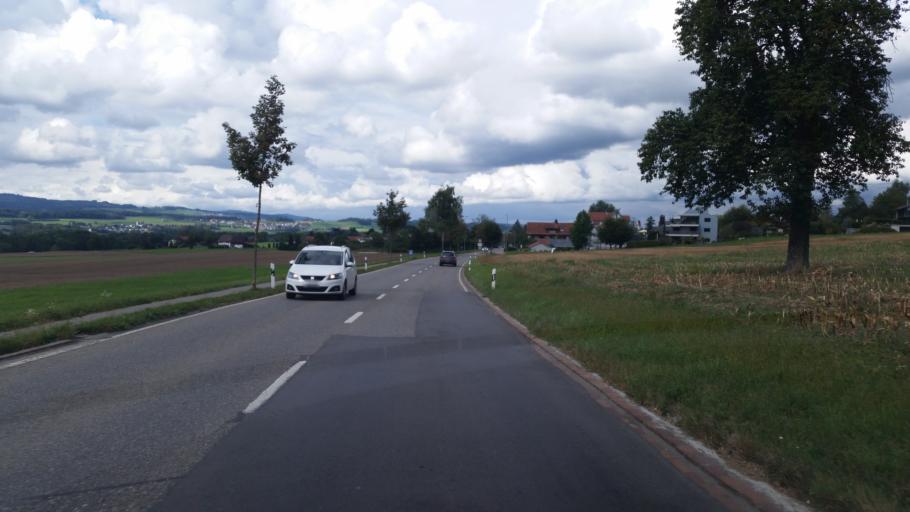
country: CH
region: Zurich
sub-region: Bezirk Affoltern
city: Obfelden / Oberlunnern
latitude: 47.2734
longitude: 8.4132
